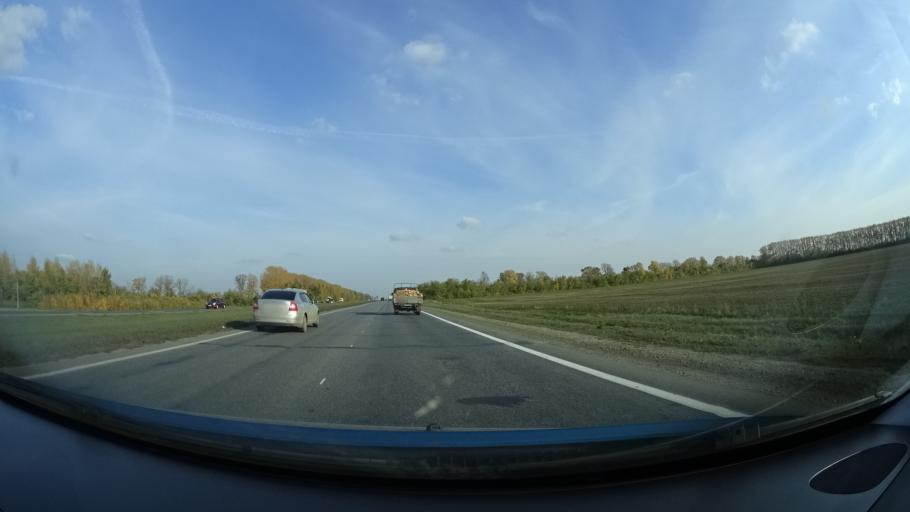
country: RU
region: Bashkortostan
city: Chishmy
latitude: 54.6588
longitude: 55.4629
